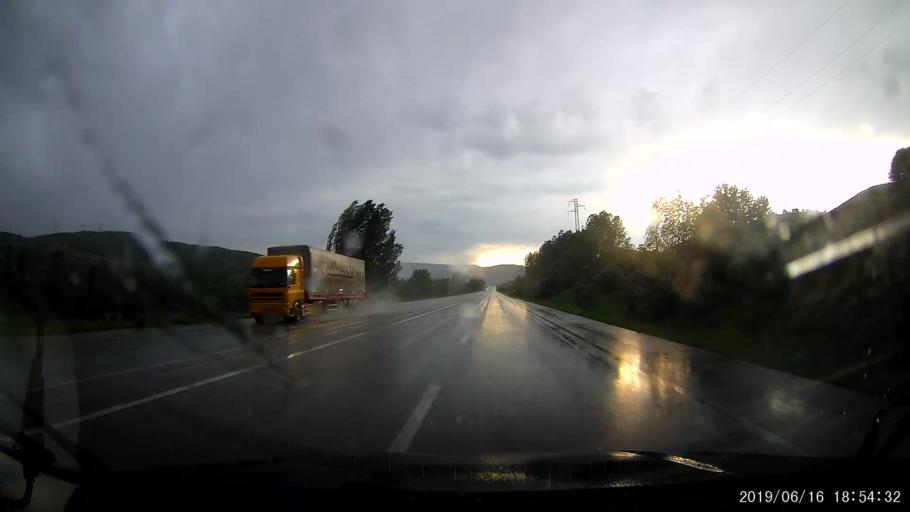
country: TR
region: Erzincan
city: Catalcam
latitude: 39.8972
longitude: 38.8515
